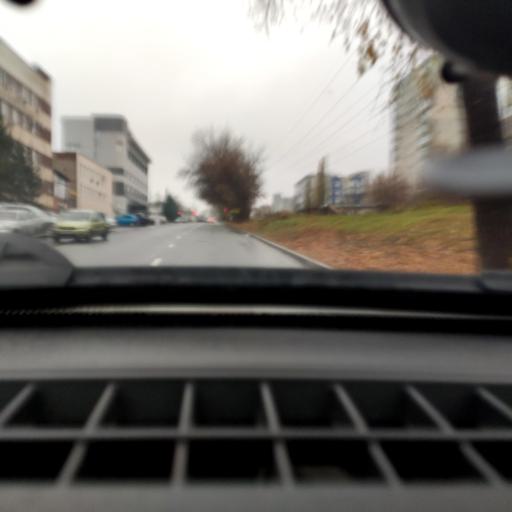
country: RU
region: Bashkortostan
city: Ufa
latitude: 54.7546
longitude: 56.0194
